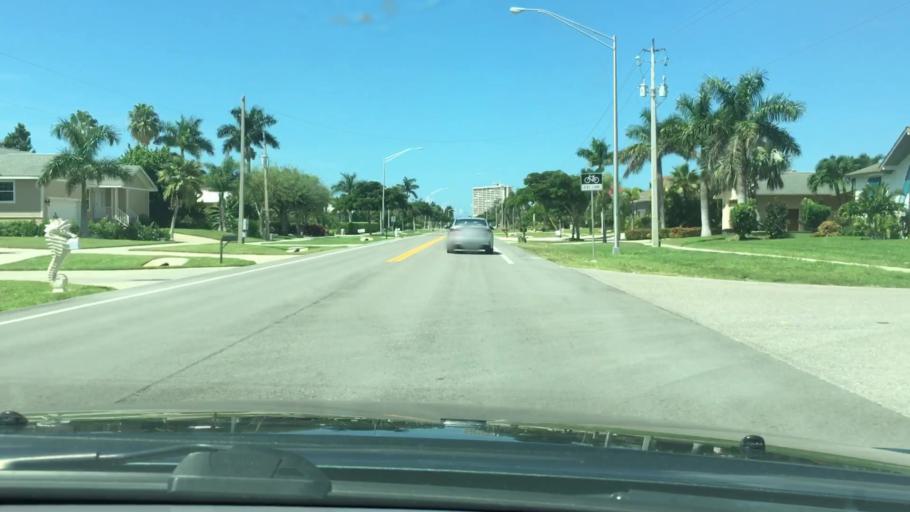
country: US
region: Florida
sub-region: Collier County
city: Marco
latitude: 25.9371
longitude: -81.7195
